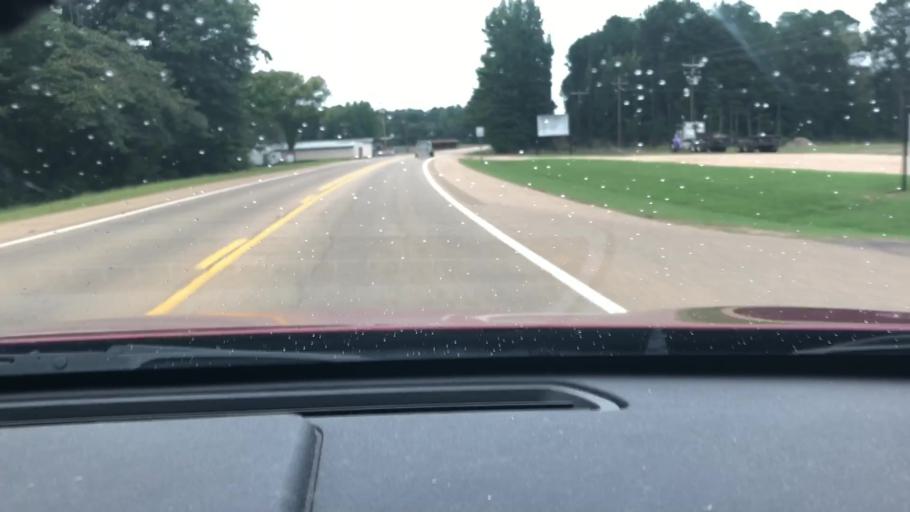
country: US
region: Arkansas
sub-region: Lafayette County
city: Stamps
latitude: 33.3675
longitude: -93.5159
